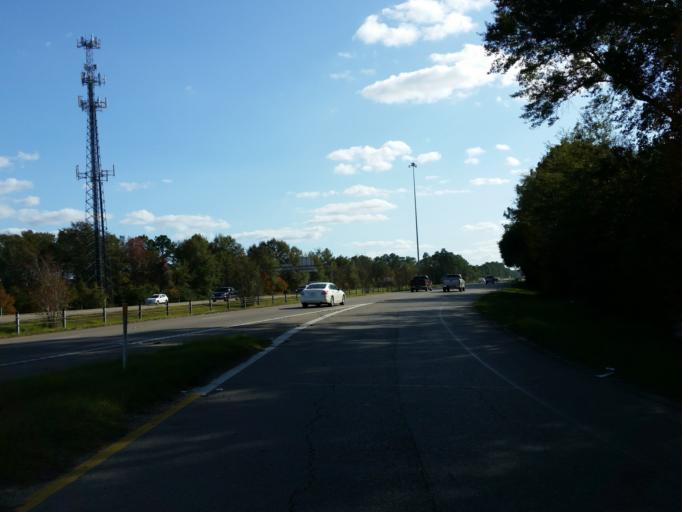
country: US
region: Mississippi
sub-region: Lamar County
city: West Hattiesburg
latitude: 31.3226
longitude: -89.3527
